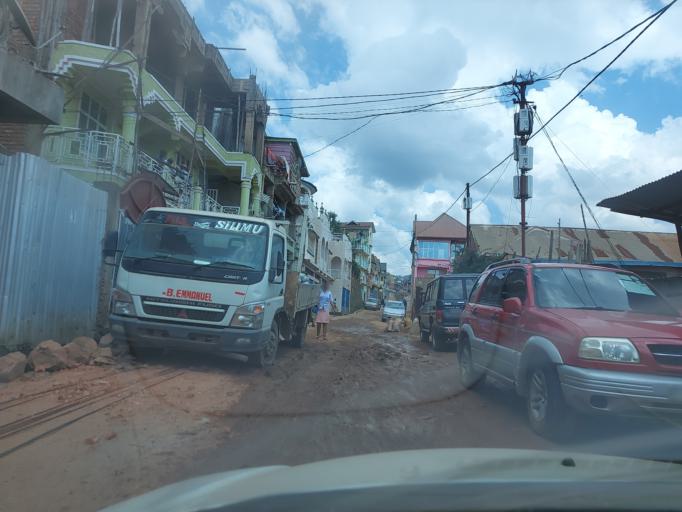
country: CD
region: South Kivu
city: Bukavu
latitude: -2.5033
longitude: 28.8640
